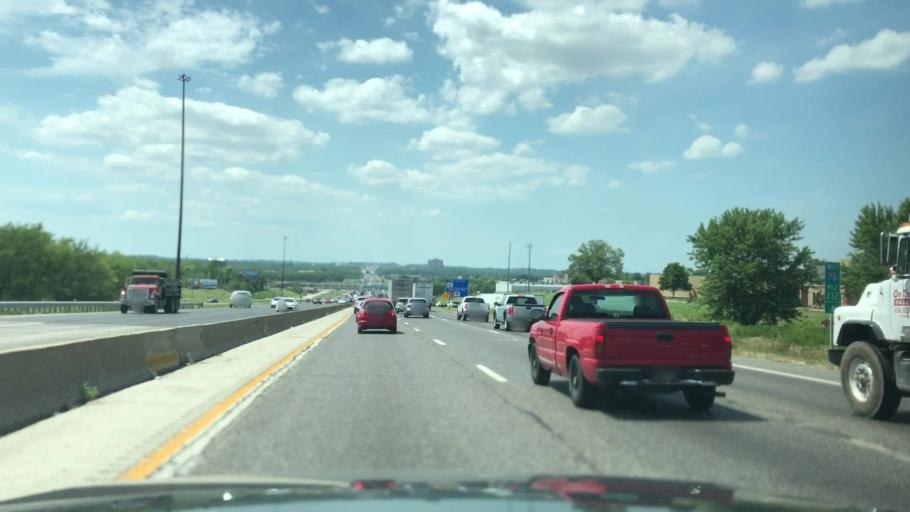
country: US
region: Missouri
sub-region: Saint Louis County
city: Bridgeton
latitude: 38.7495
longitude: -90.4420
